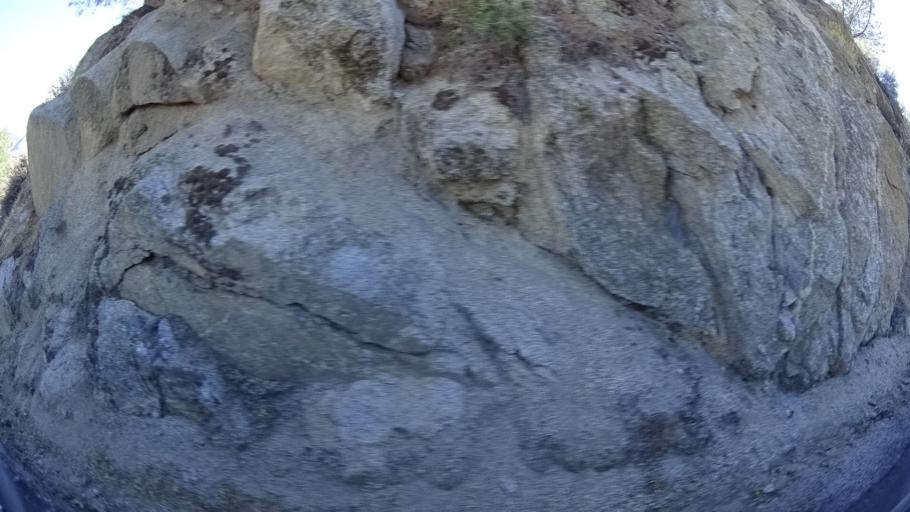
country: US
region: California
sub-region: Kern County
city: Bodfish
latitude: 35.5947
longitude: -118.5078
